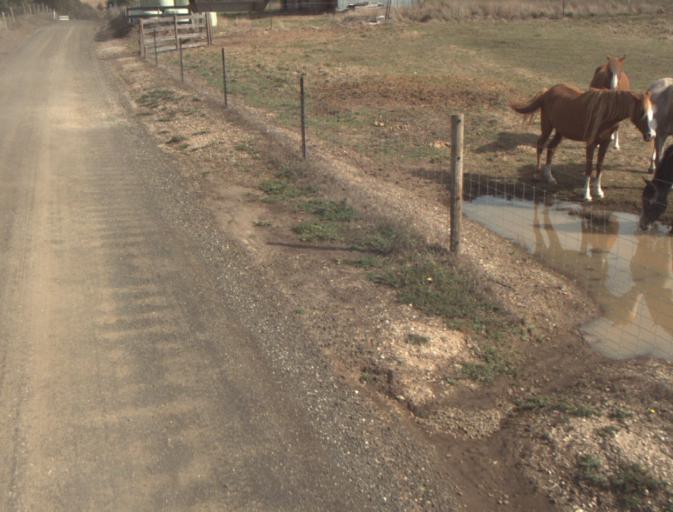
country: AU
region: Tasmania
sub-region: Launceston
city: Mayfield
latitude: -41.1889
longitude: 147.1907
